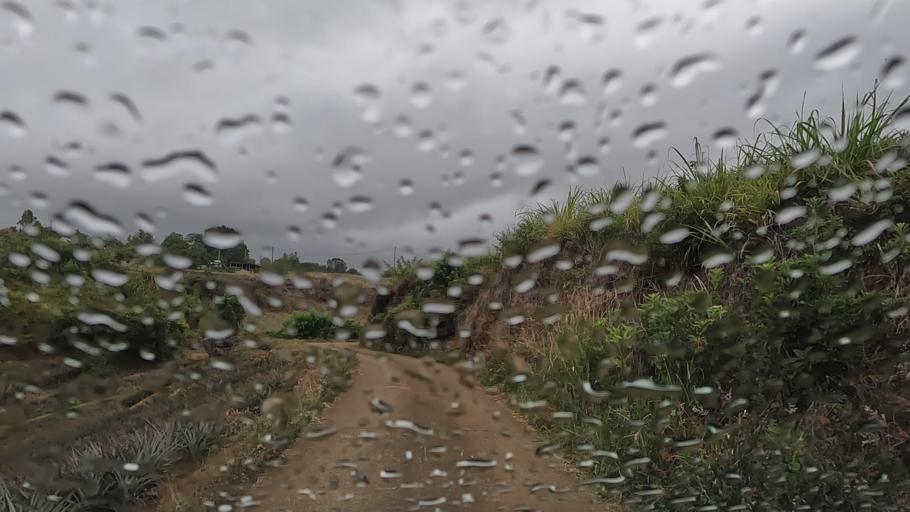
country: RE
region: Reunion
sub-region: Reunion
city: Le Tampon
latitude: -21.2914
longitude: 55.5480
